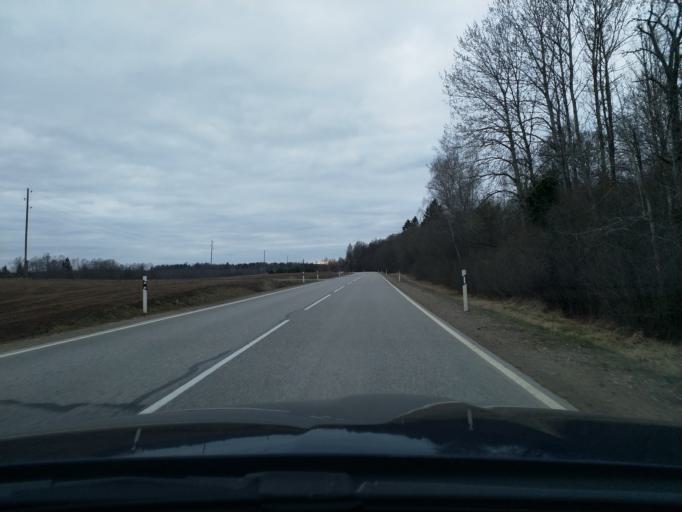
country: LV
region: Kuldigas Rajons
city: Kuldiga
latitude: 56.9610
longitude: 22.0776
